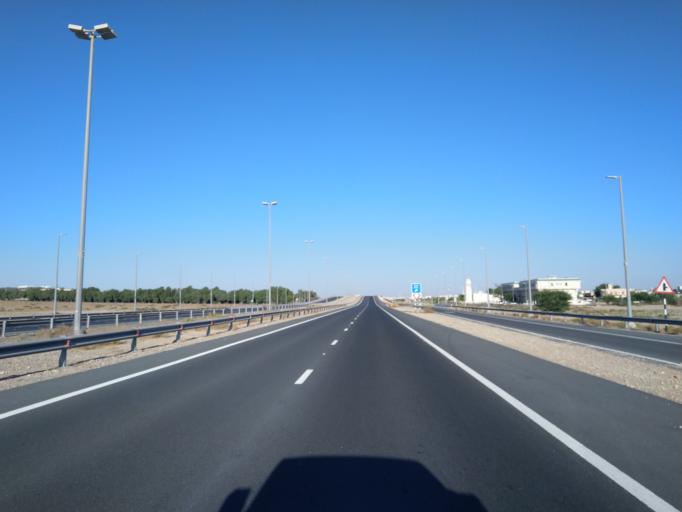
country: OM
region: Al Buraimi
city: Al Buraymi
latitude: 24.5116
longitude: 55.4814
